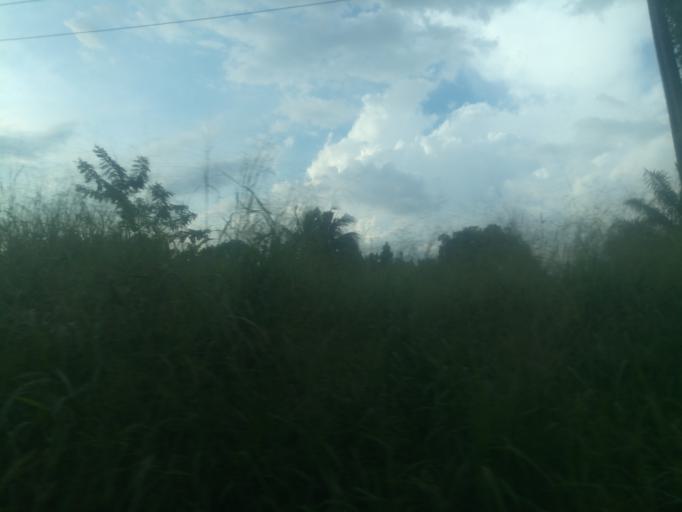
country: NG
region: Oyo
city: Ibadan
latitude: 7.3795
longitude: 3.8463
